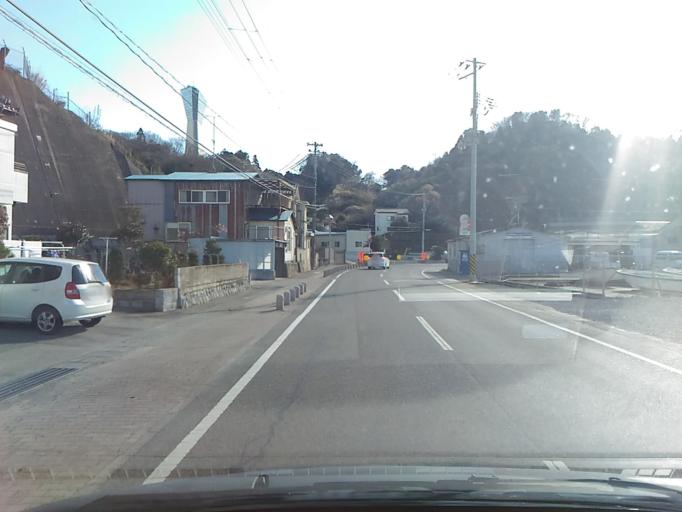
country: JP
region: Fukushima
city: Iwaki
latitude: 36.9413
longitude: 140.9164
